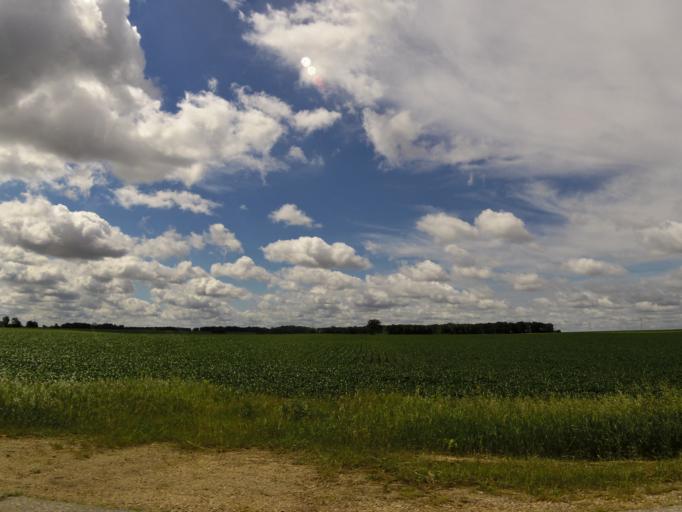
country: US
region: Minnesota
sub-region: Fillmore County
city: Spring Valley
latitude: 43.7106
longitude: -92.4571
